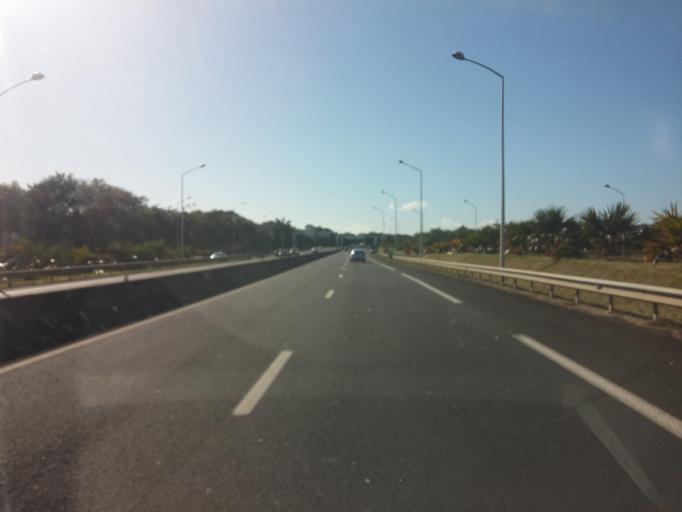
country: RE
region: Reunion
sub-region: Reunion
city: Sainte-Marie
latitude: -20.8972
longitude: 55.5113
